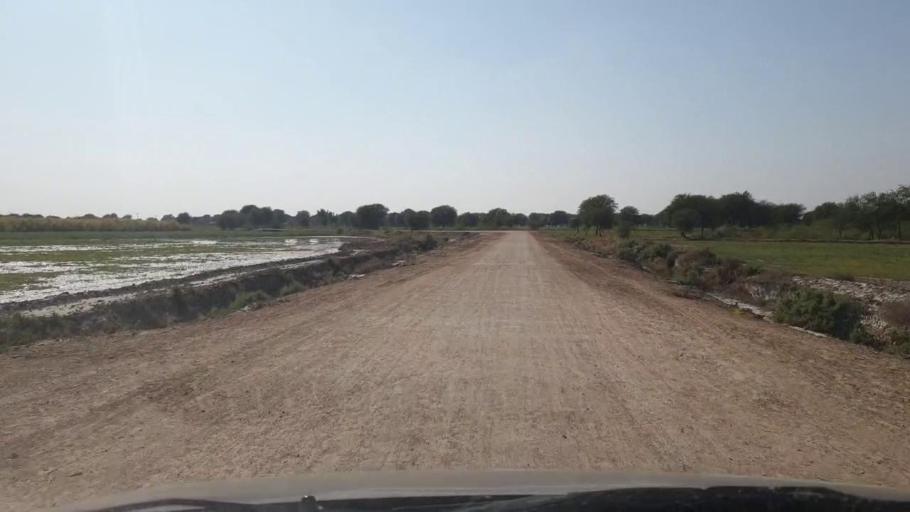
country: PK
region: Sindh
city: Samaro
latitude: 25.2151
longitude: 69.2735
